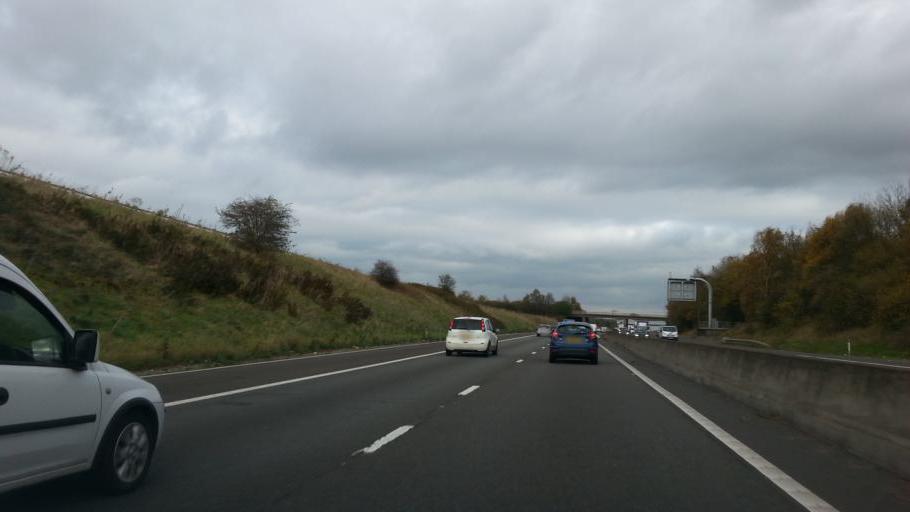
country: GB
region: England
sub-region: Warwickshire
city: Kingsbury
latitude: 52.5924
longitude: -1.6537
